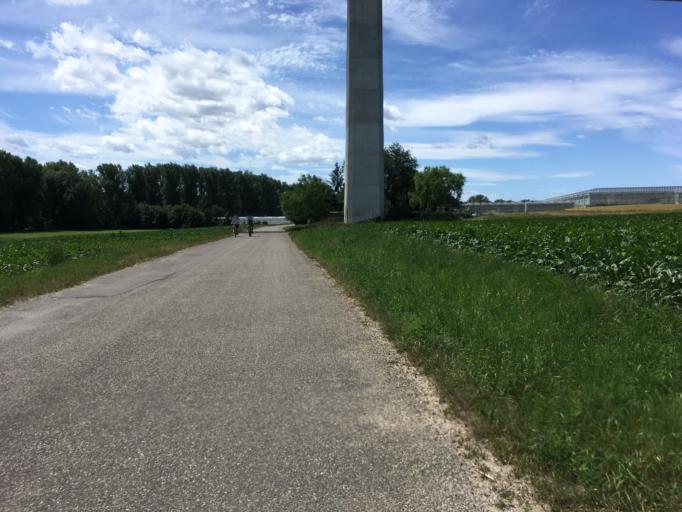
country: DE
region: Baden-Wuerttemberg
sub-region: Regierungsbezirk Stuttgart
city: Oberriexingen
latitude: 48.9245
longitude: 8.9993
